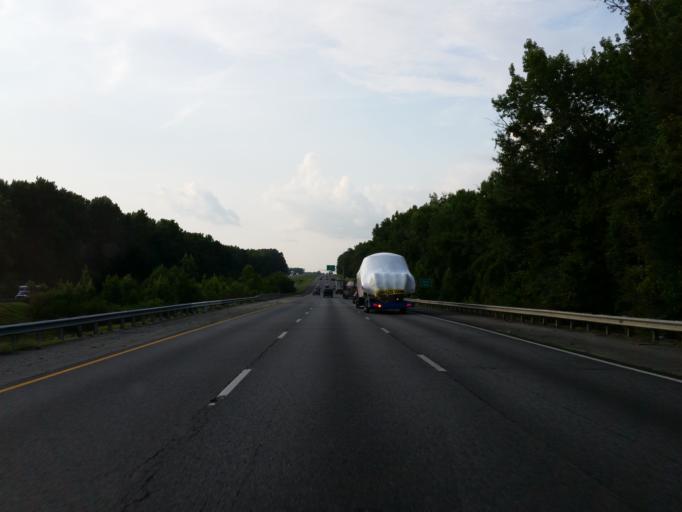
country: US
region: Georgia
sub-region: Houston County
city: Perry
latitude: 32.5307
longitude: -83.7433
